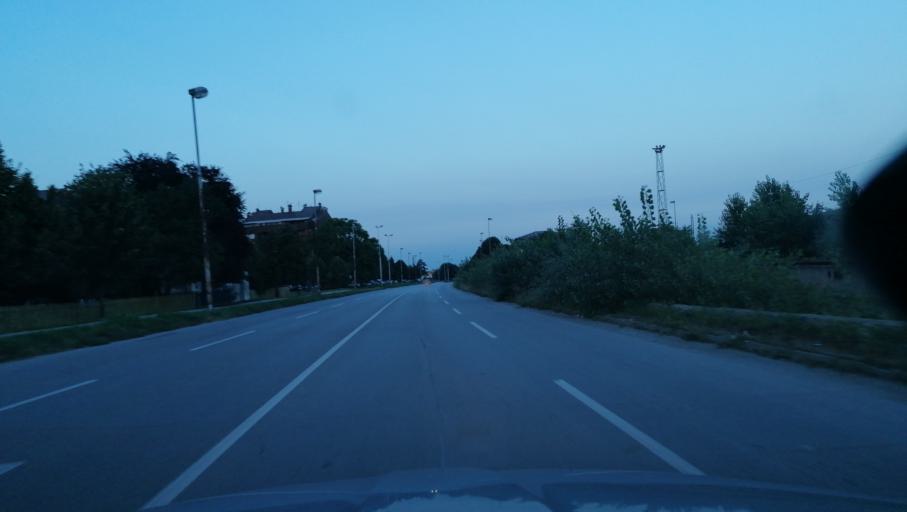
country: RS
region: Central Serbia
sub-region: Kolubarski Okrug
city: Valjevo
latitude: 44.2702
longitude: 19.9014
